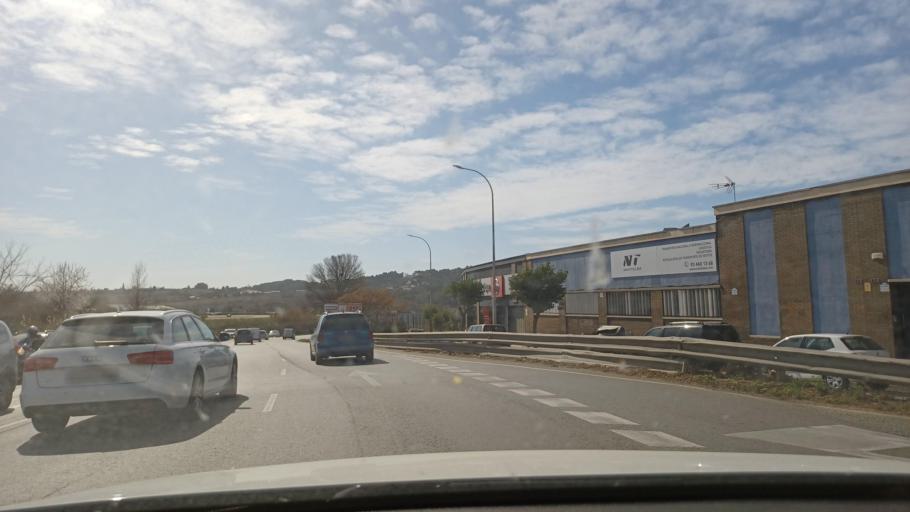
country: ES
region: Catalonia
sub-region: Provincia de Barcelona
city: Sabadell
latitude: 41.5268
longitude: 2.1023
